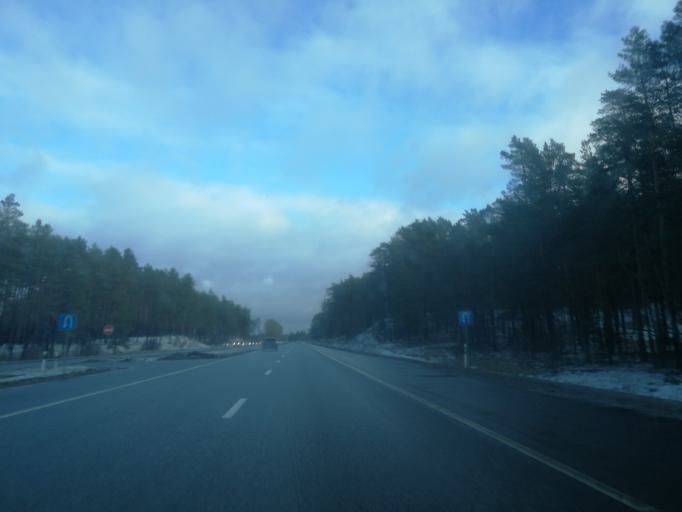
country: LV
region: Garkalne
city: Garkalne
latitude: 57.0350
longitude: 24.3866
